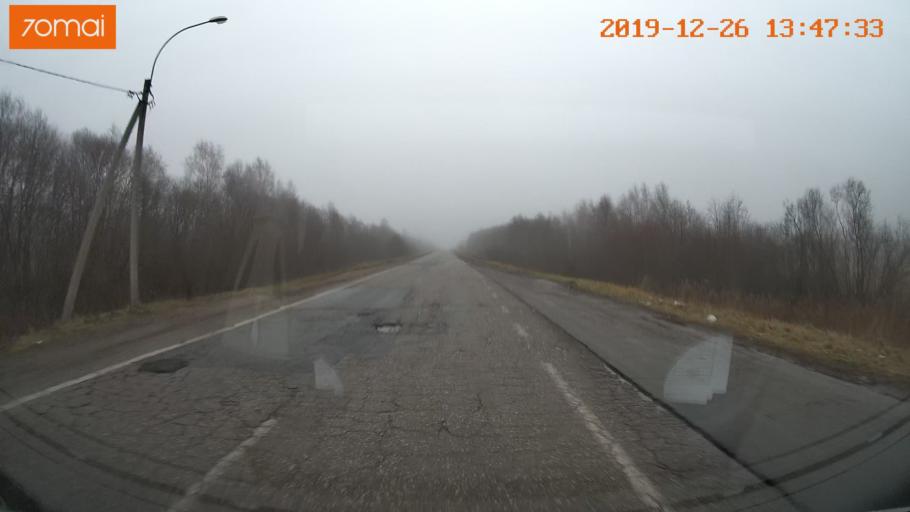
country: RU
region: Vologda
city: Sheksna
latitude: 58.6840
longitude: 38.5353
